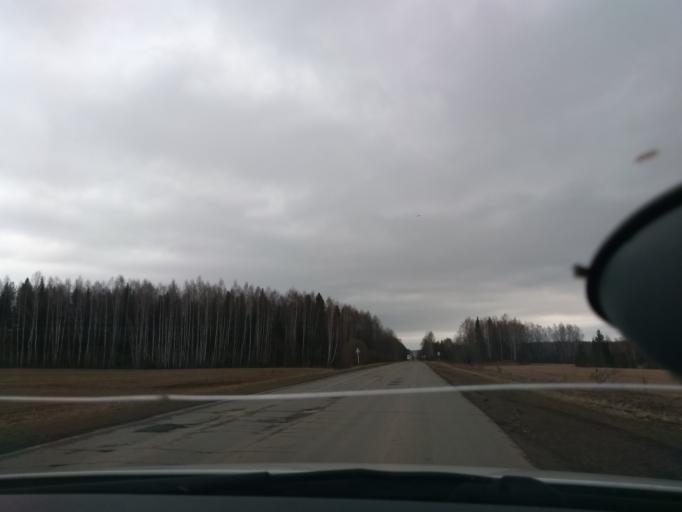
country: RU
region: Perm
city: Kungur
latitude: 57.3642
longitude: 56.8224
